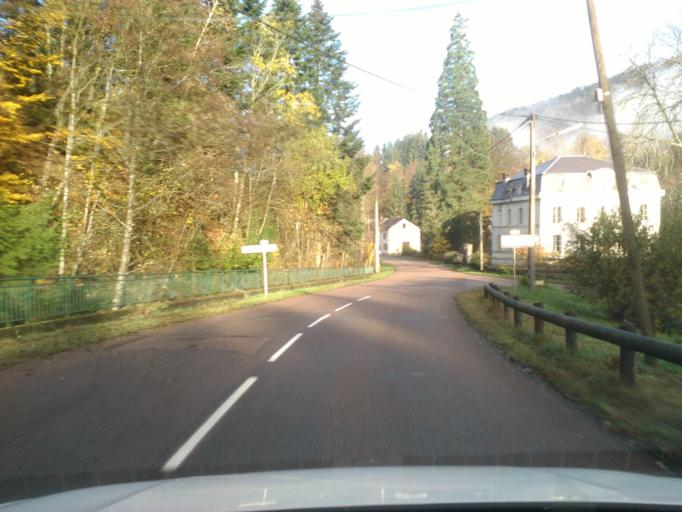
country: FR
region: Lorraine
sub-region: Departement des Vosges
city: Senones
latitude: 48.4179
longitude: 7.0453
